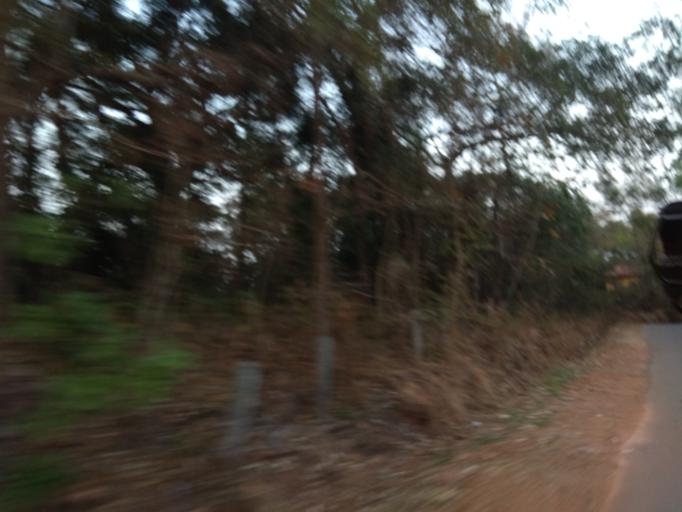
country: IN
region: Karnataka
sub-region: Dakshina Kannada
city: Mangalore
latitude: 12.9275
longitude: 74.8717
